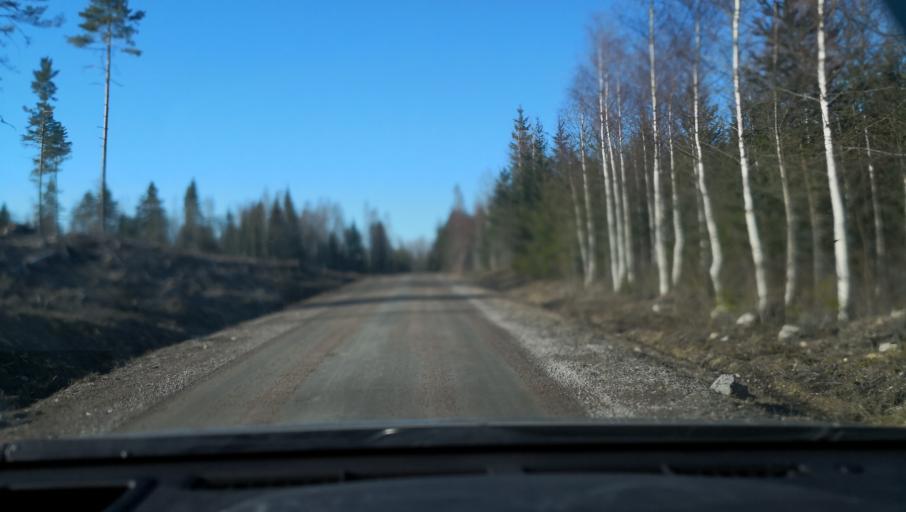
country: SE
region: Vaestmanland
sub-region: Sala Kommun
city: Sala
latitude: 60.1594
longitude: 16.6288
